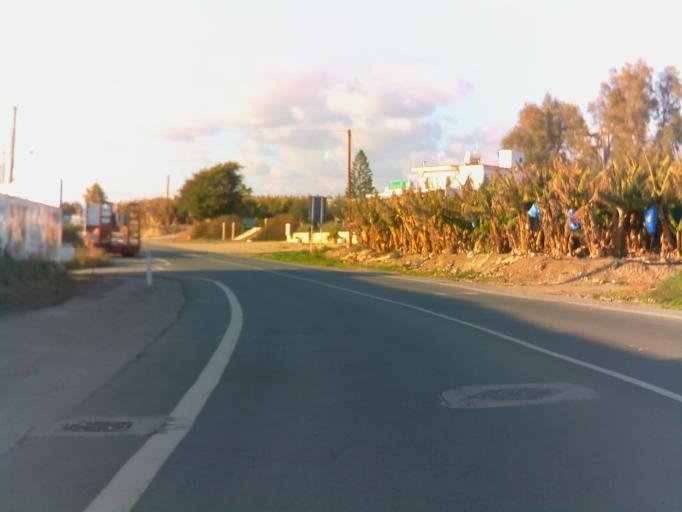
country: CY
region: Pafos
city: Kissonerga
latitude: 34.8193
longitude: 32.3951
